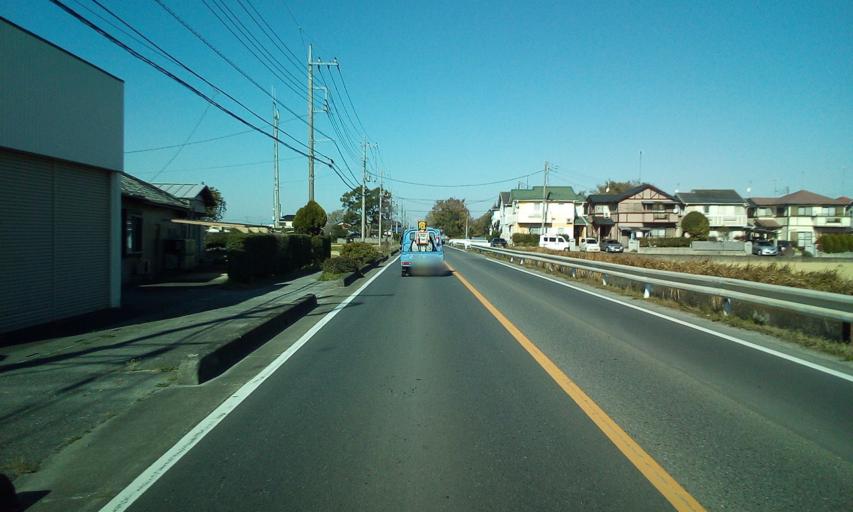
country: JP
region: Saitama
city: Kasukabe
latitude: 36.0212
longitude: 139.7902
